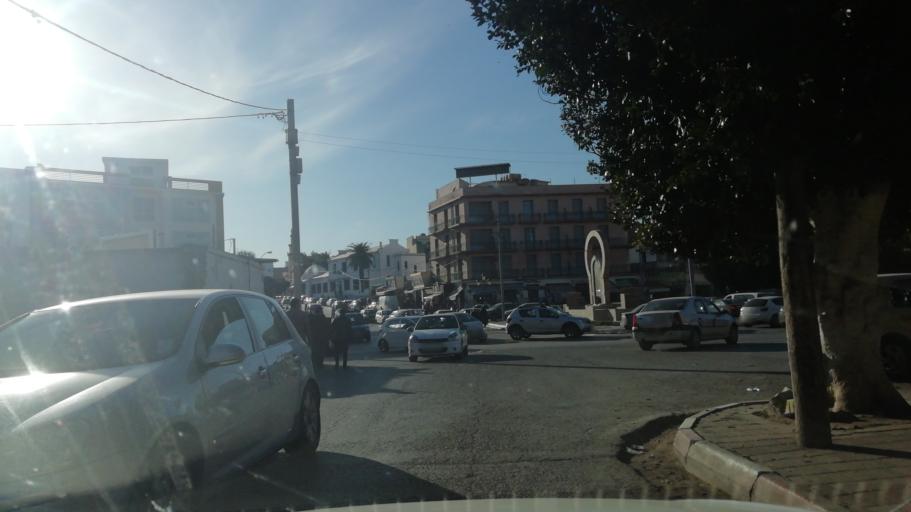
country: DZ
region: Oran
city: Oran
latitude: 35.6931
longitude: -0.6446
